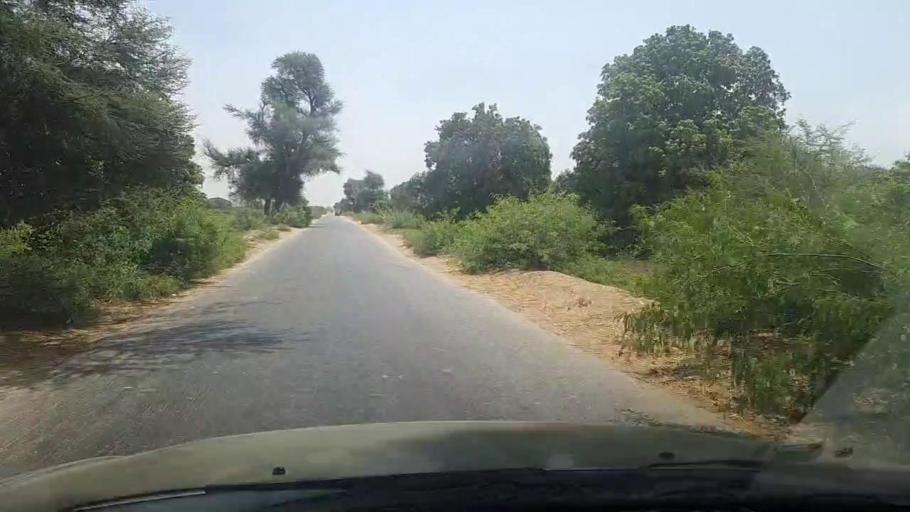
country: PK
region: Sindh
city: Tando Jam
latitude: 25.2784
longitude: 68.6143
